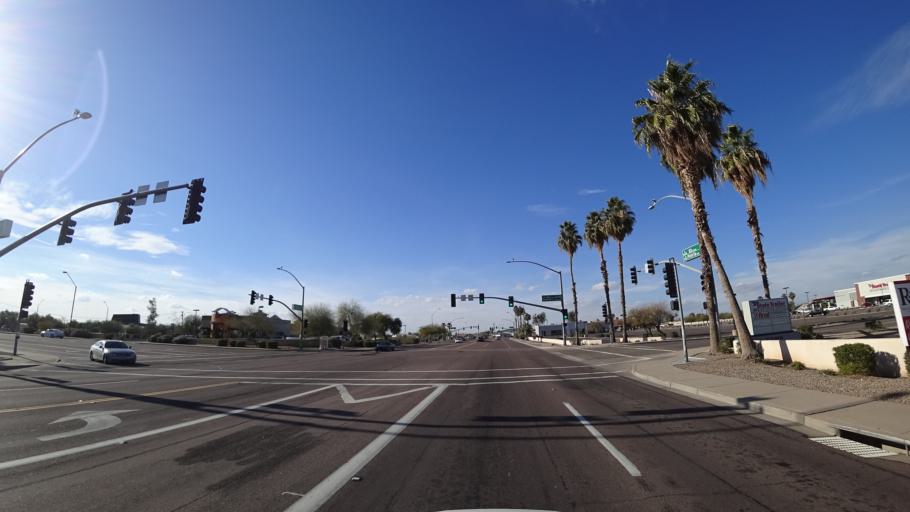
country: US
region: Arizona
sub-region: Maricopa County
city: Peoria
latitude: 33.5817
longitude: -112.2357
